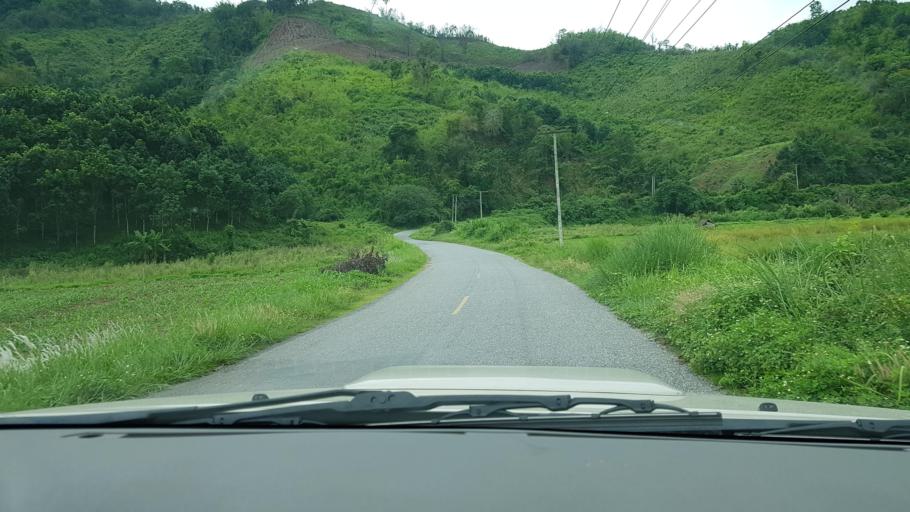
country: LA
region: Loungnamtha
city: Muang Nale
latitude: 20.3704
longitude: 101.7189
